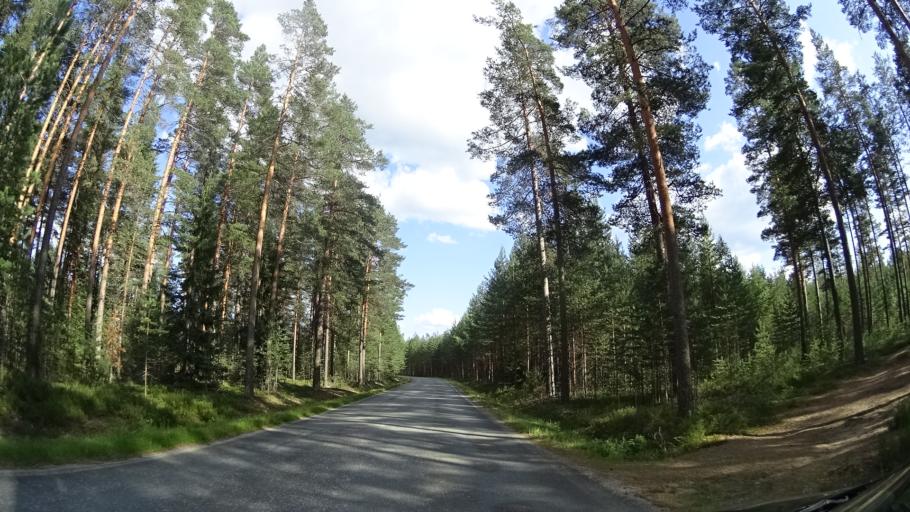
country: FI
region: Uusimaa
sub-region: Helsinki
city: Kaerkoelae
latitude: 60.7407
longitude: 24.0886
